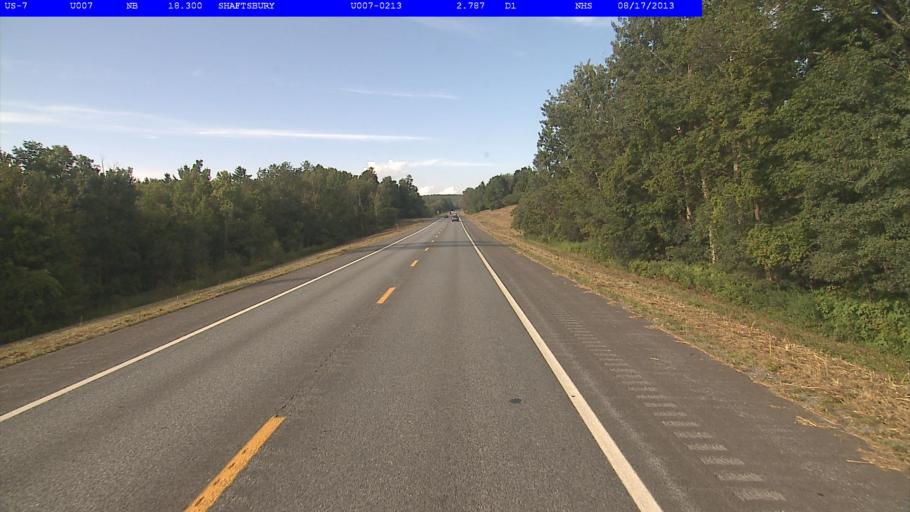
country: US
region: Vermont
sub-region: Bennington County
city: North Bennington
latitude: 42.9678
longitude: -73.1627
